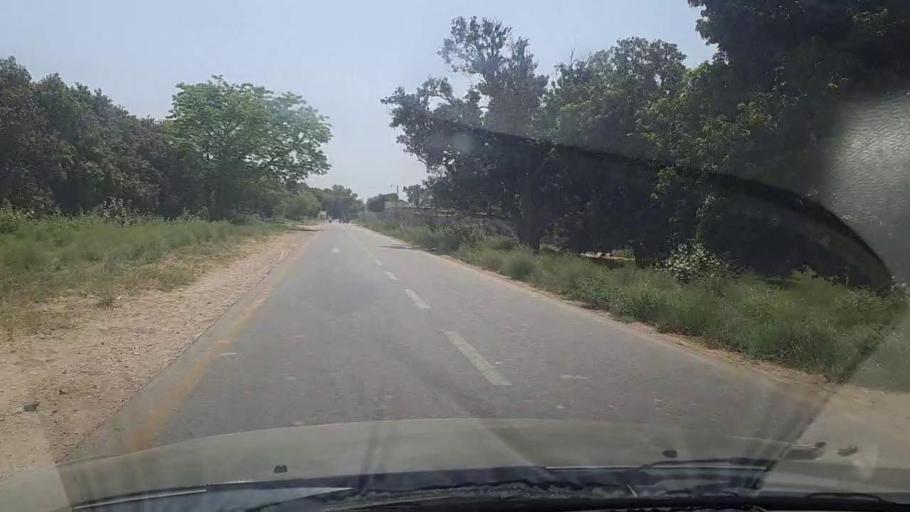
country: PK
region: Sindh
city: Tando Jam
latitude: 25.3434
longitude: 68.5194
